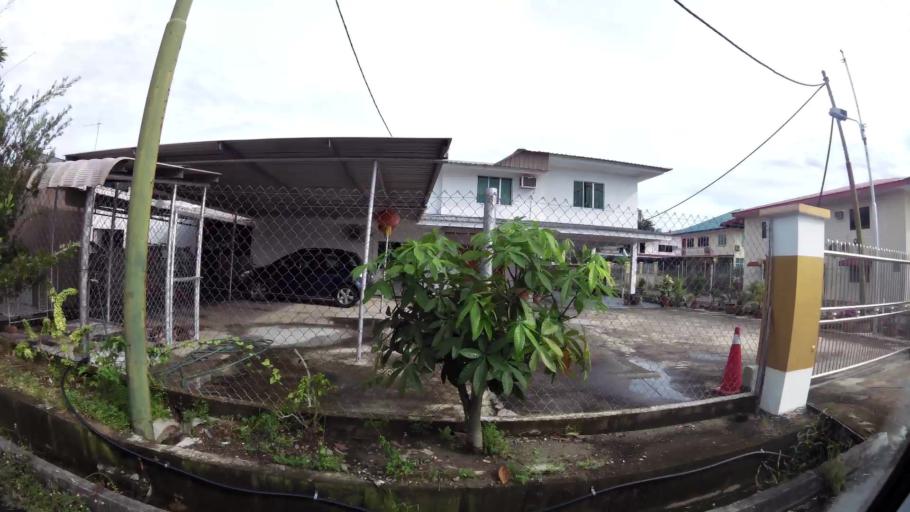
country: BN
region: Belait
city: Seria
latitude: 4.6156
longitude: 114.3618
